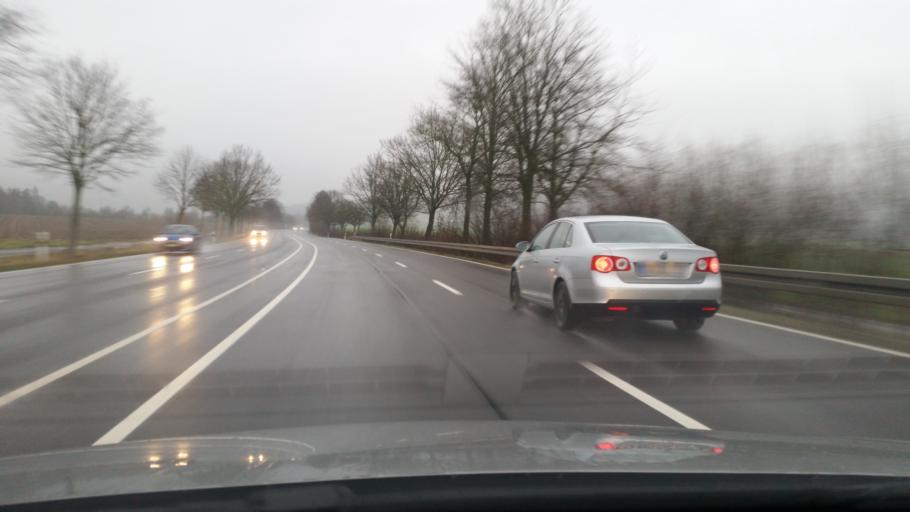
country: DE
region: Lower Saxony
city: Springe
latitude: 52.1824
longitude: 9.5270
